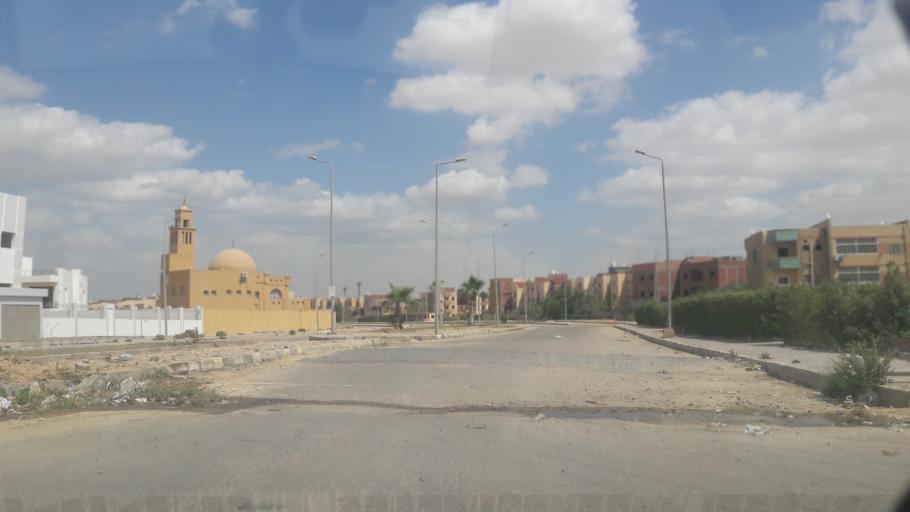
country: EG
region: Al Jizah
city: Madinat Sittah Uktubar
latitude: 29.9340
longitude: 31.0580
